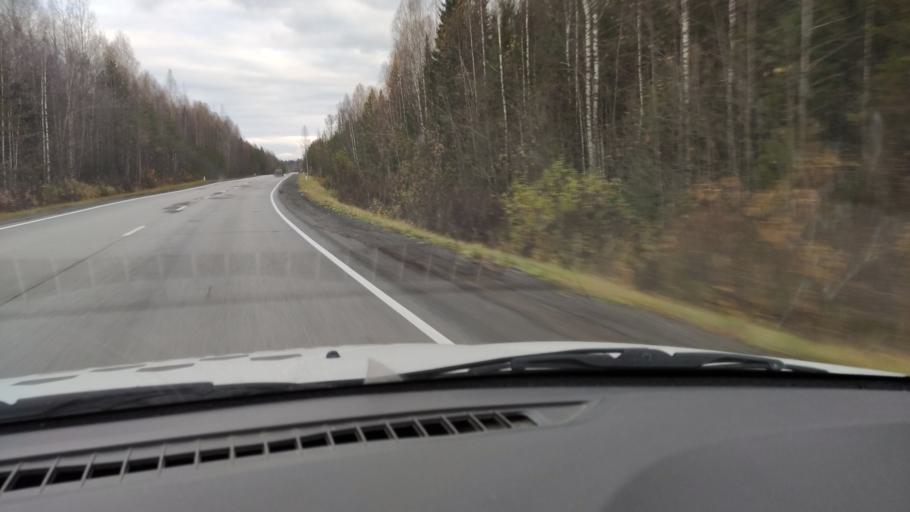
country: RU
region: Kirov
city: Chernaya Kholunitsa
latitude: 58.8681
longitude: 51.5619
